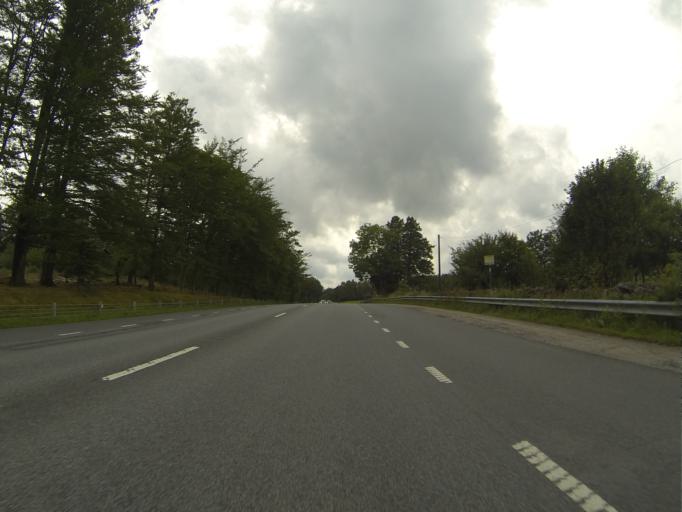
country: SE
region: Skane
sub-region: Hassleholms Kommun
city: Vinslov
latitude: 55.9411
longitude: 13.8564
